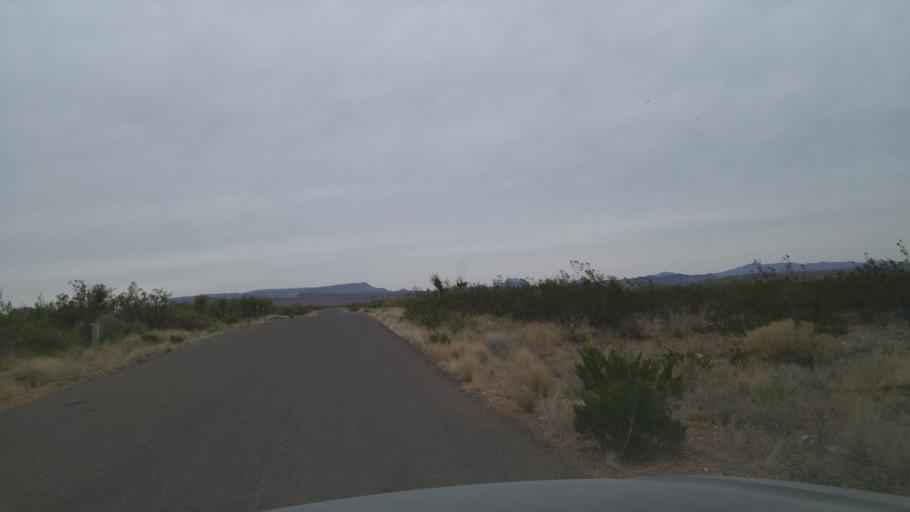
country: US
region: Texas
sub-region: Brewster County
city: Alpine
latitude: 29.4965
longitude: -103.3694
